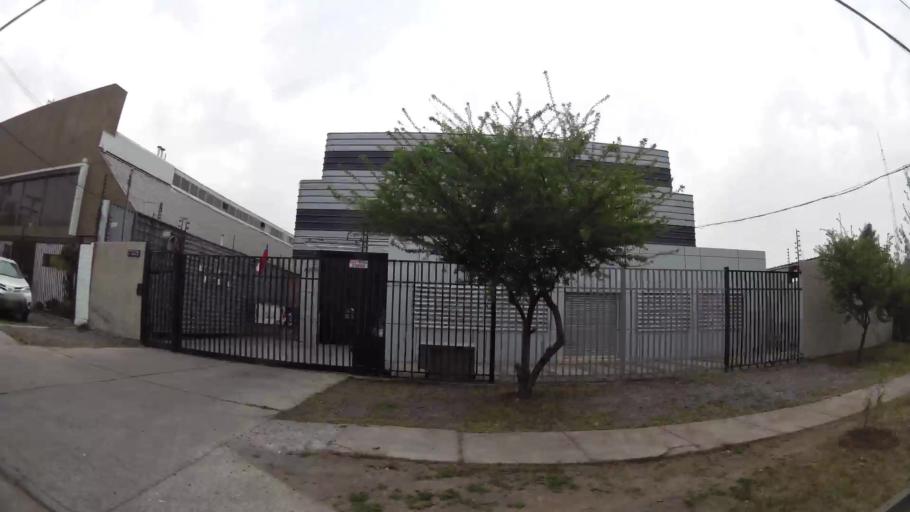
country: CL
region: Santiago Metropolitan
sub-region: Provincia de Santiago
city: Villa Presidente Frei, Nunoa, Santiago, Chile
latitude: -33.4932
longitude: -70.6078
